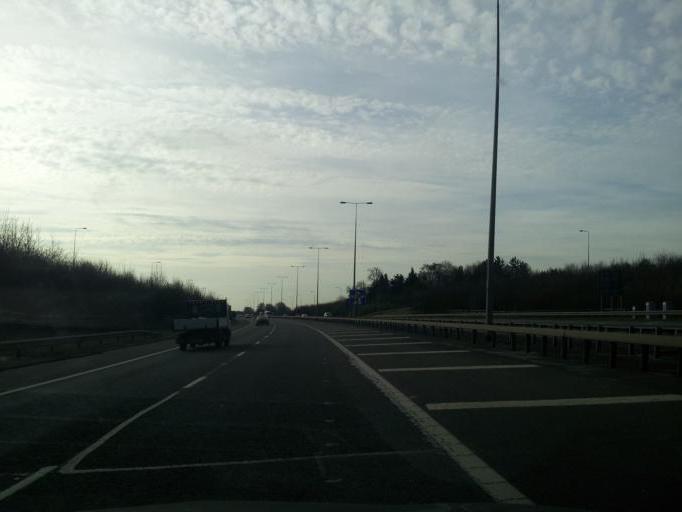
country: GB
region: England
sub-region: Cambridgeshire
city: Great Stukeley
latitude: 52.3620
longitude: -0.2552
